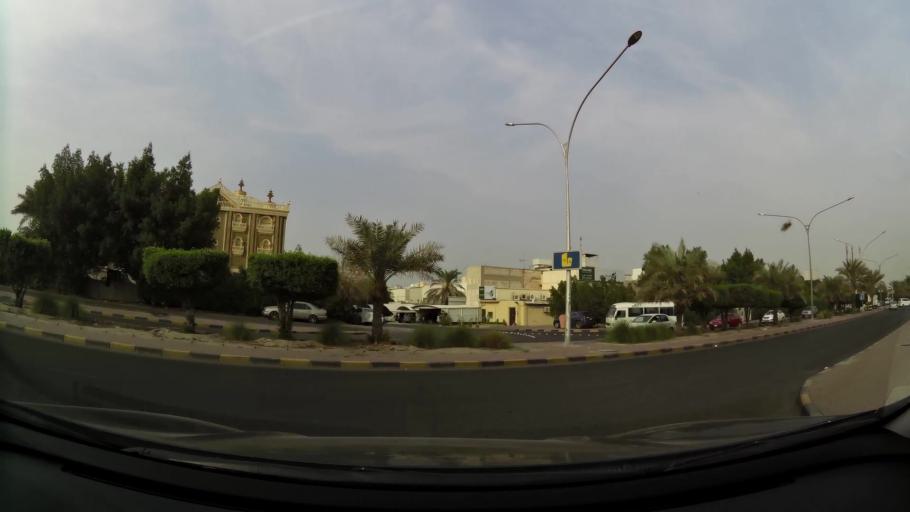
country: KW
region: Al Farwaniyah
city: Al Farwaniyah
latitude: 29.2968
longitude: 47.9664
